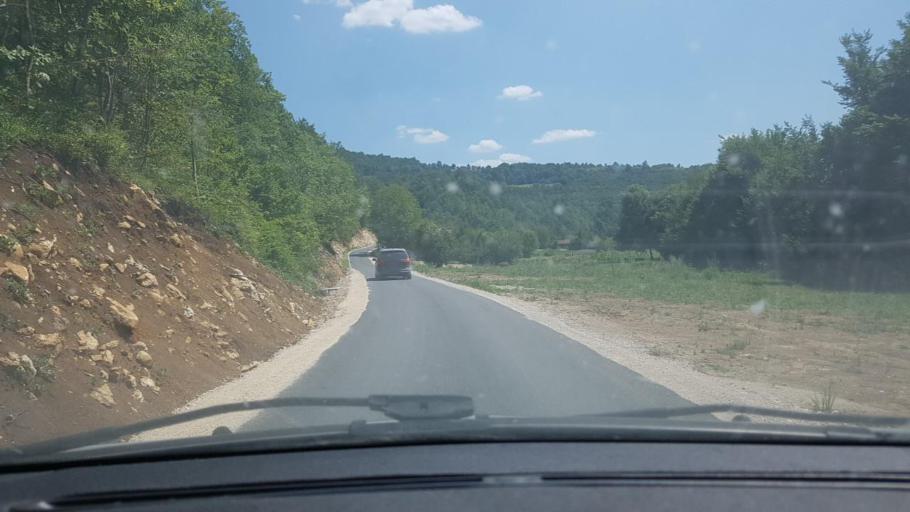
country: BA
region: Federation of Bosnia and Herzegovina
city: Orasac
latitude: 44.6422
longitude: 16.0386
